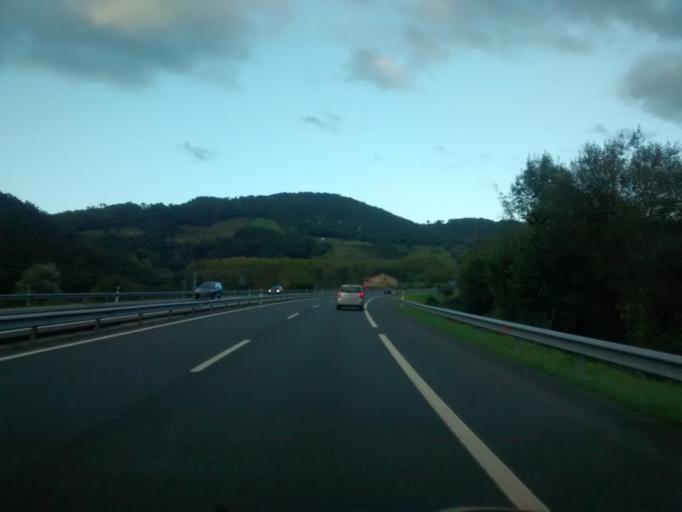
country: ES
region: Basque Country
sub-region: Provincia de Guipuzcoa
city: Zumaia
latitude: 43.2821
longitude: -2.2371
